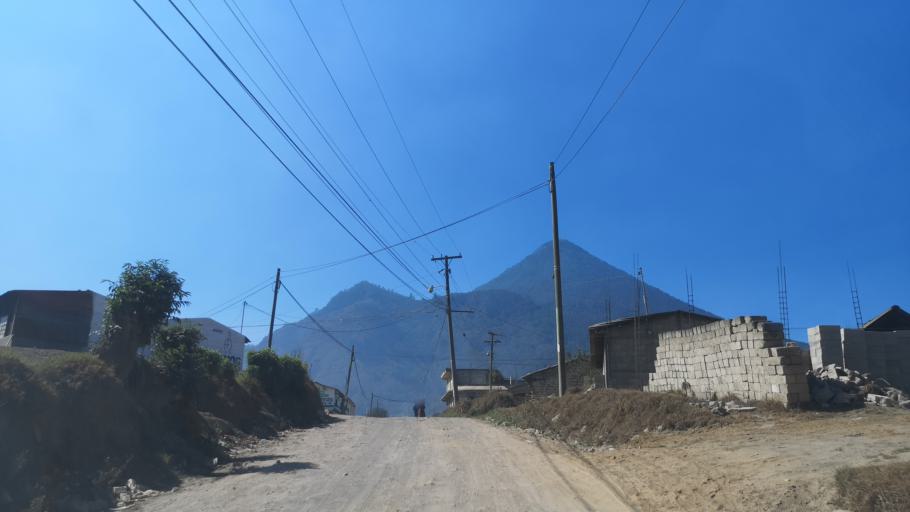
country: GT
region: Quetzaltenango
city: Quetzaltenango
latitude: 14.7955
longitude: -91.5436
